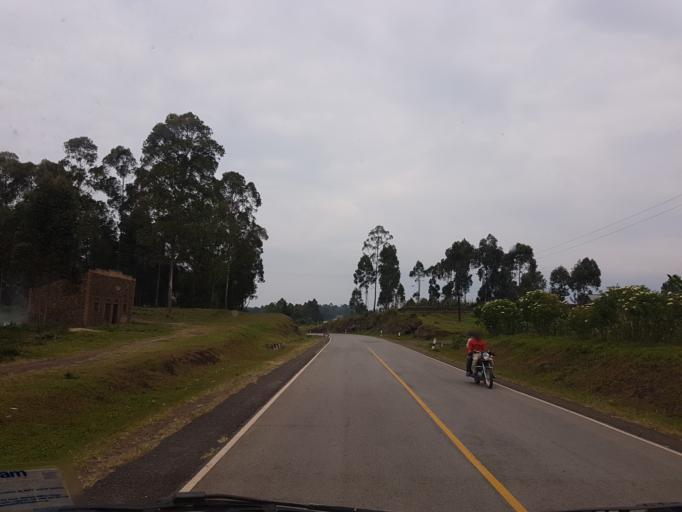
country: UG
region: Western Region
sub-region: Kisoro District
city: Kisoro
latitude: -1.3182
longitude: 29.7267
